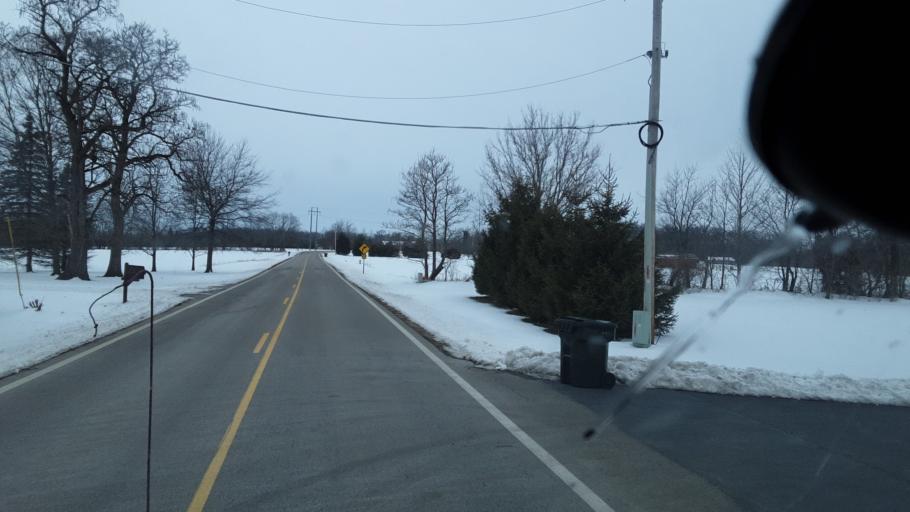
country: US
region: Ohio
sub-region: Madison County
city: Plain City
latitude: 40.1449
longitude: -83.3390
